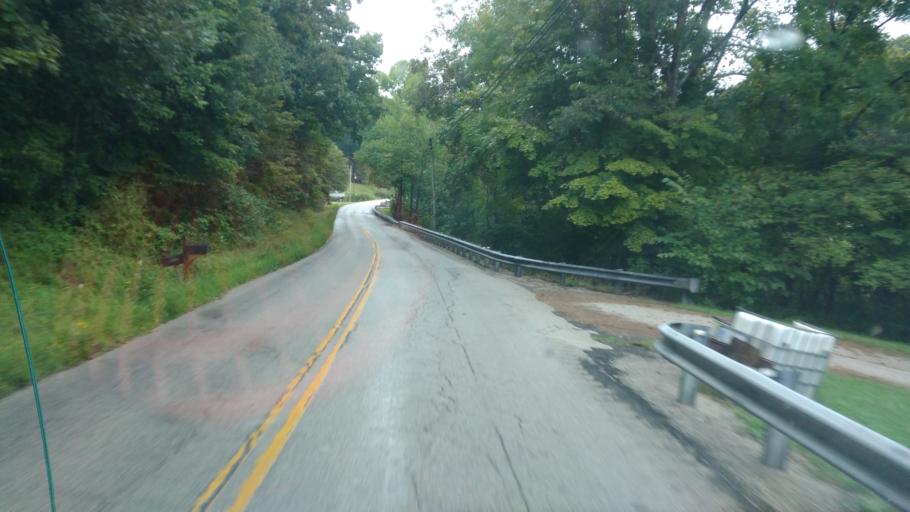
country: US
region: Kentucky
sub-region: Fleming County
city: Flemingsburg
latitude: 38.4500
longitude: -83.5162
